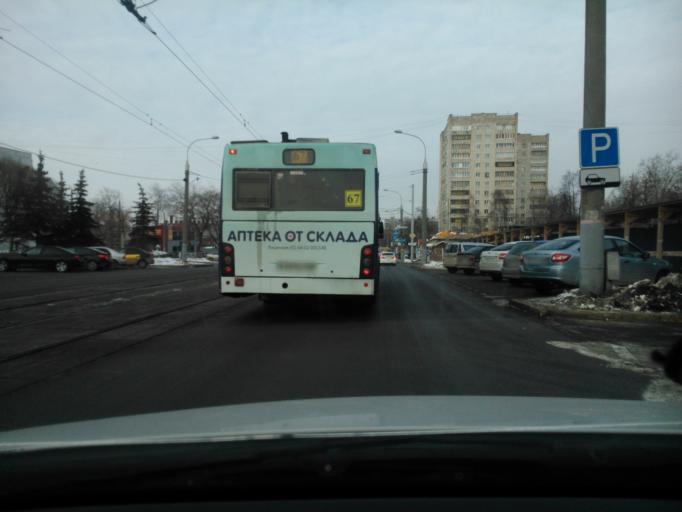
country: RU
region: Perm
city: Perm
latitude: 58.0032
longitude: 56.2232
